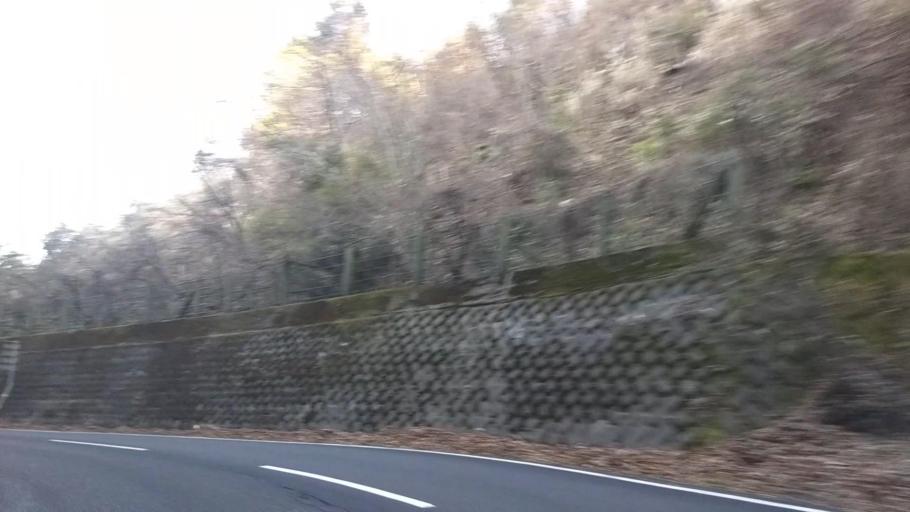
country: JP
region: Yamanashi
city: Uenohara
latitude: 35.5489
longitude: 139.1529
